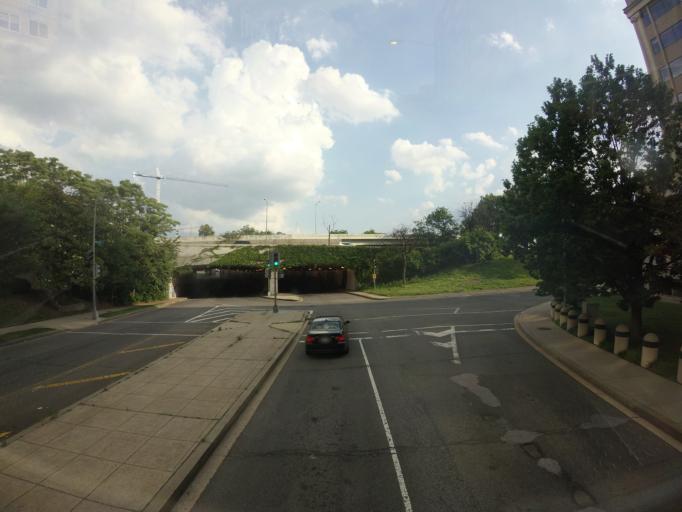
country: US
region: Washington, D.C.
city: Washington, D.C.
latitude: 38.8830
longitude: -77.0281
